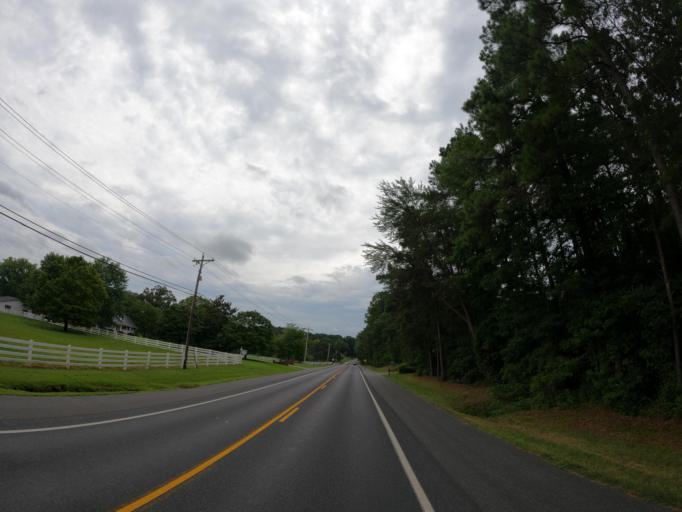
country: US
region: Maryland
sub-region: Saint Mary's County
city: California
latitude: 38.2347
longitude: -76.5217
